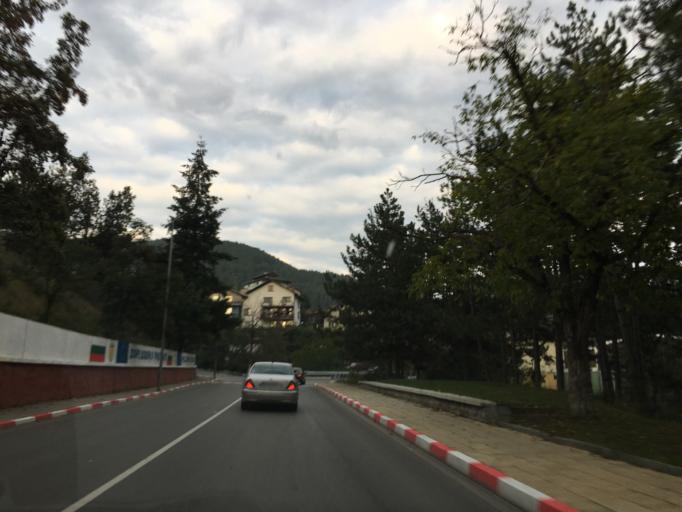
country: BG
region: Sofiya
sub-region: Obshtina Svoge
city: Svoge
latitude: 42.9537
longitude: 23.3620
